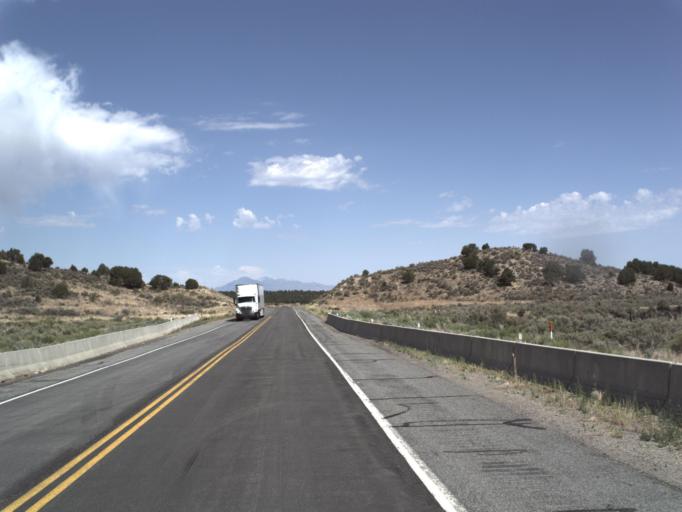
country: US
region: Utah
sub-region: Utah County
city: Eagle Mountain
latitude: 39.9923
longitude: -112.2686
